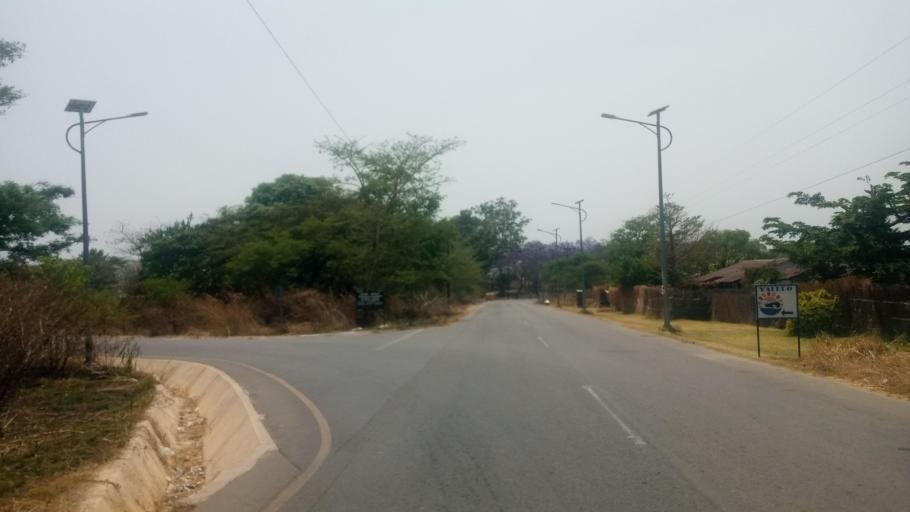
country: ZM
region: Lusaka
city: Lusaka
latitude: -15.4562
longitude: 28.4400
